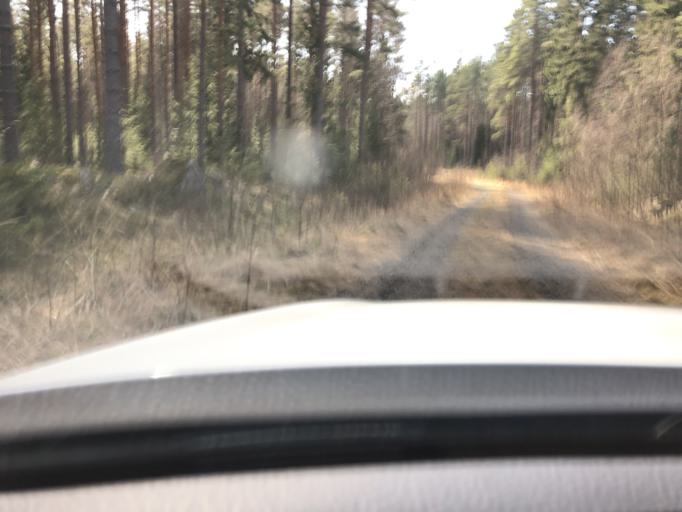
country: SE
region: Uppsala
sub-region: Heby Kommun
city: OEstervala
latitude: 60.3343
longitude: 17.1709
